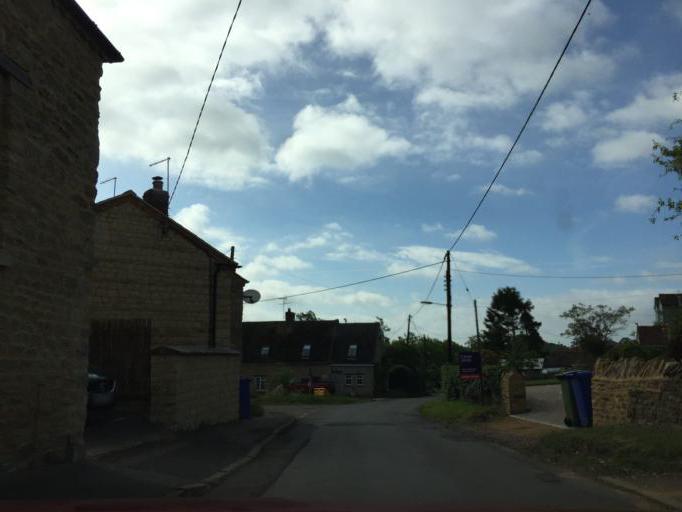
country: GB
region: England
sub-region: Northamptonshire
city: Blisworth
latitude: 52.1423
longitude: -0.9405
